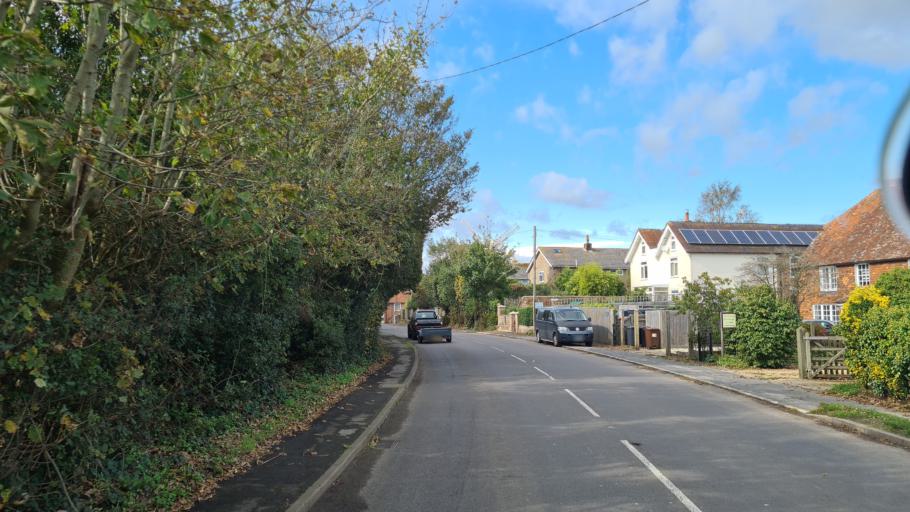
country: GB
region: England
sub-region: East Sussex
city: Bodle Street
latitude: 50.8846
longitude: 0.3421
